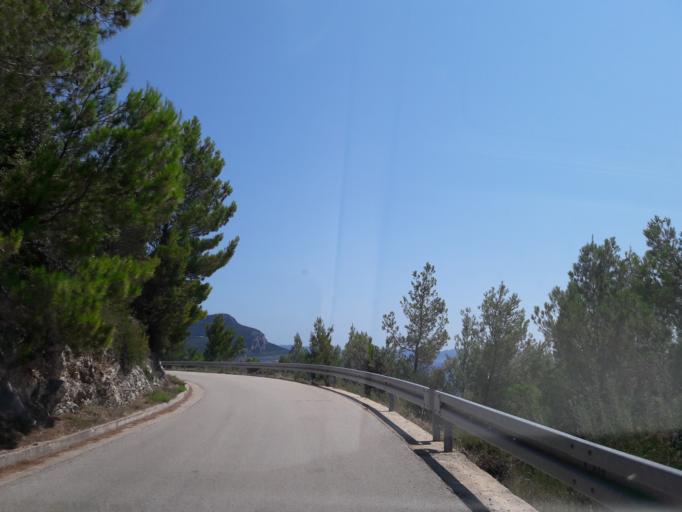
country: HR
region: Dubrovacko-Neretvanska
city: Blato
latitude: 42.9087
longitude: 17.4217
